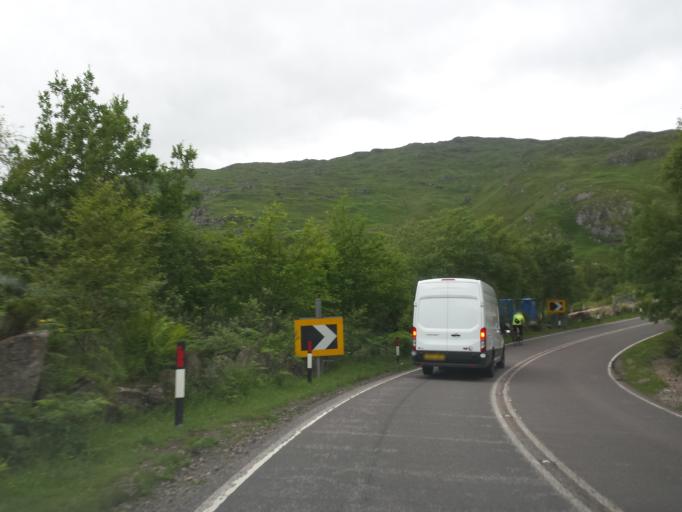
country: GB
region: Scotland
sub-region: Argyll and Bute
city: Isle Of Mull
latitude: 56.8834
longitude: -5.6309
